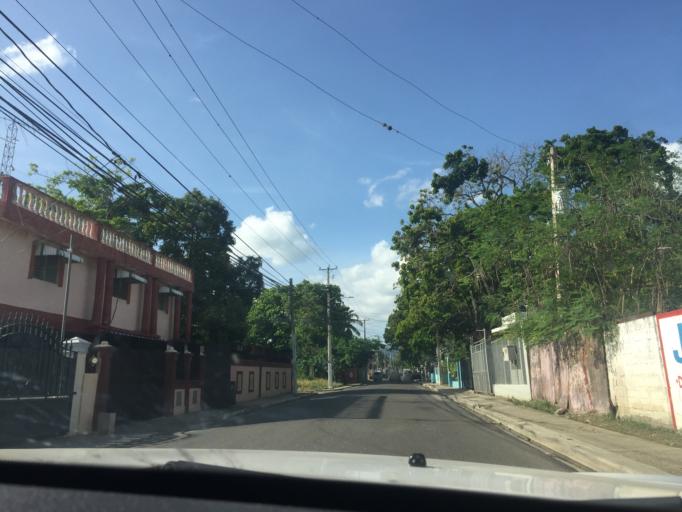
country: DO
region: Santiago
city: Santiago de los Caballeros
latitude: 19.4683
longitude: -70.6587
